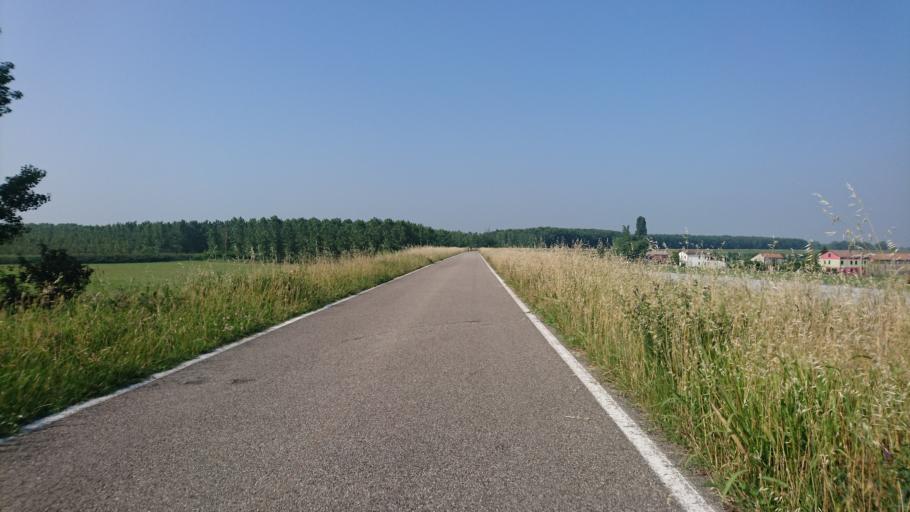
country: IT
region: Veneto
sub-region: Provincia di Rovigo
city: Bergantino
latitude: 45.0524
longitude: 11.2452
